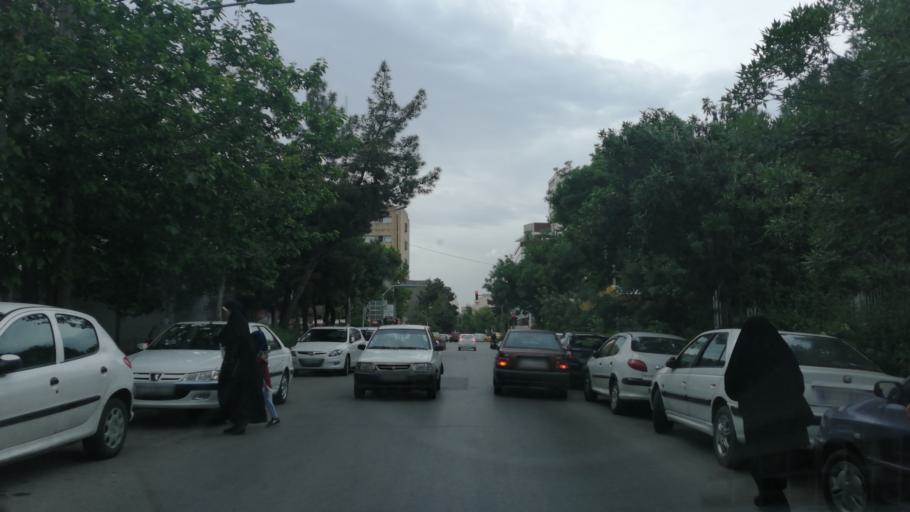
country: IR
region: Razavi Khorasan
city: Mashhad
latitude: 36.2875
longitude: 59.5780
